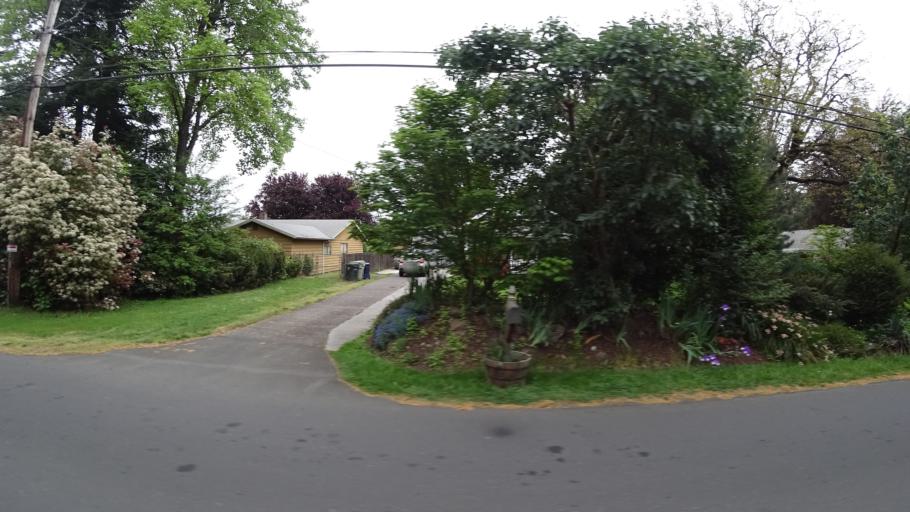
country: US
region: Oregon
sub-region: Washington County
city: Aloha
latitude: 45.5008
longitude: -122.8701
